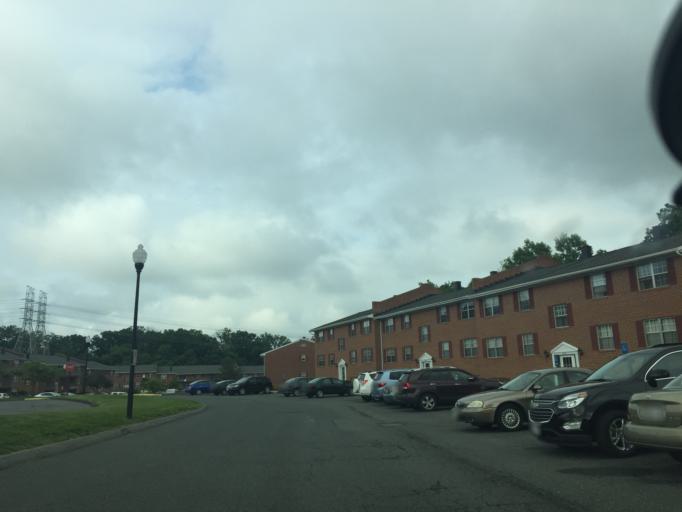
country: US
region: Maryland
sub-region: Baltimore County
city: Perry Hall
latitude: 39.3943
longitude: -76.4891
